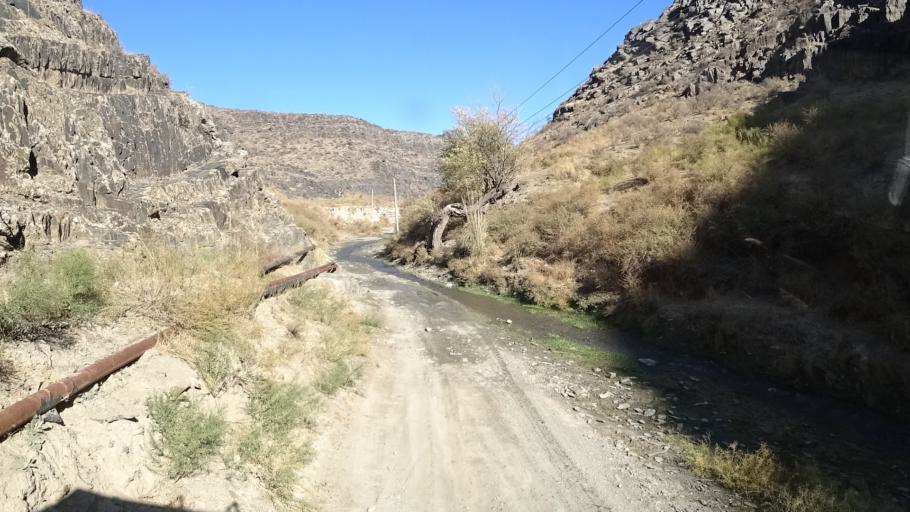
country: UZ
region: Navoiy
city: Nurota
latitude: 40.3072
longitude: 65.6197
